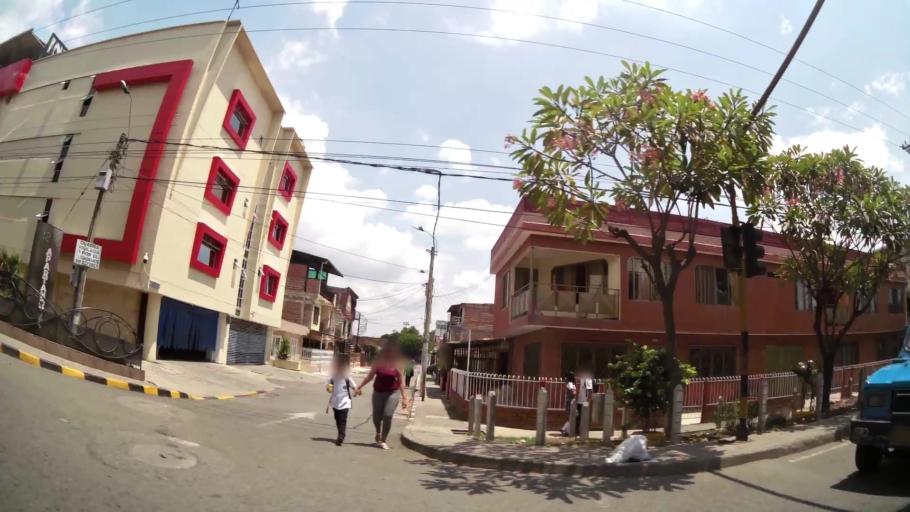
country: CO
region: Valle del Cauca
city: Cali
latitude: 3.4485
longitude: -76.4832
